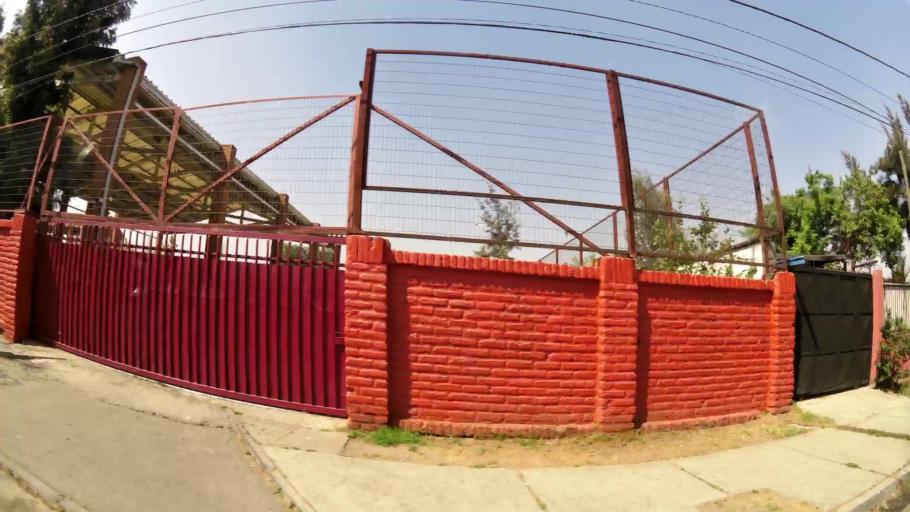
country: CL
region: Santiago Metropolitan
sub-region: Provincia de Santiago
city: La Pintana
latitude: -33.5512
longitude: -70.5981
